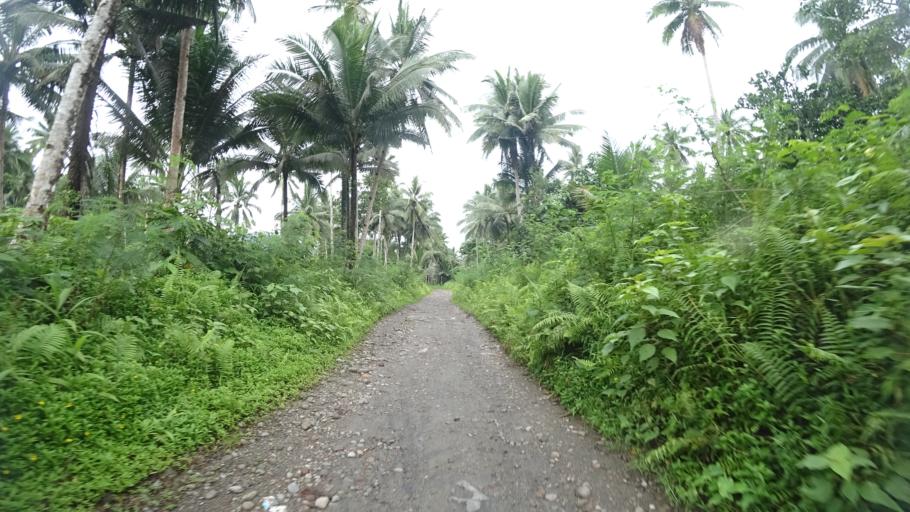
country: PH
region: Eastern Visayas
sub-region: Province of Leyte
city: Bugho
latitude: 10.8274
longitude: 124.9040
